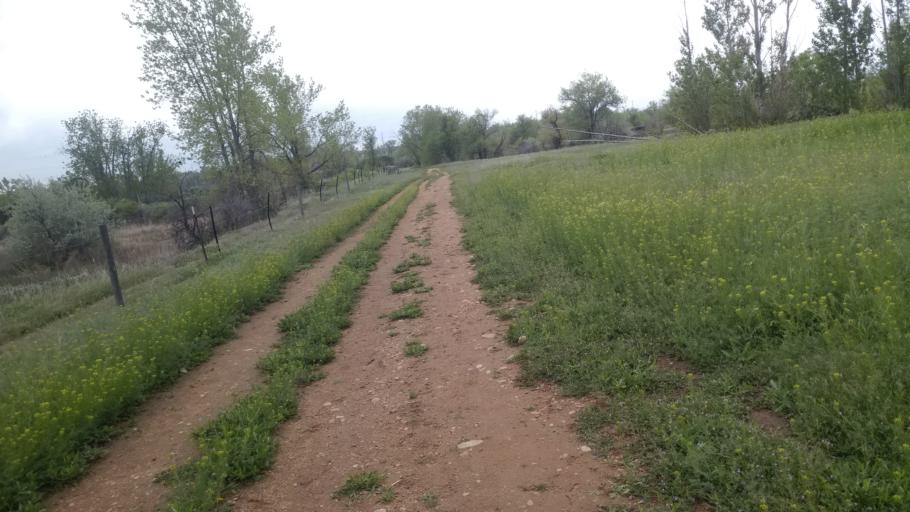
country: US
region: Colorado
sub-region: Boulder County
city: Gunbarrel
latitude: 40.0427
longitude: -105.1878
